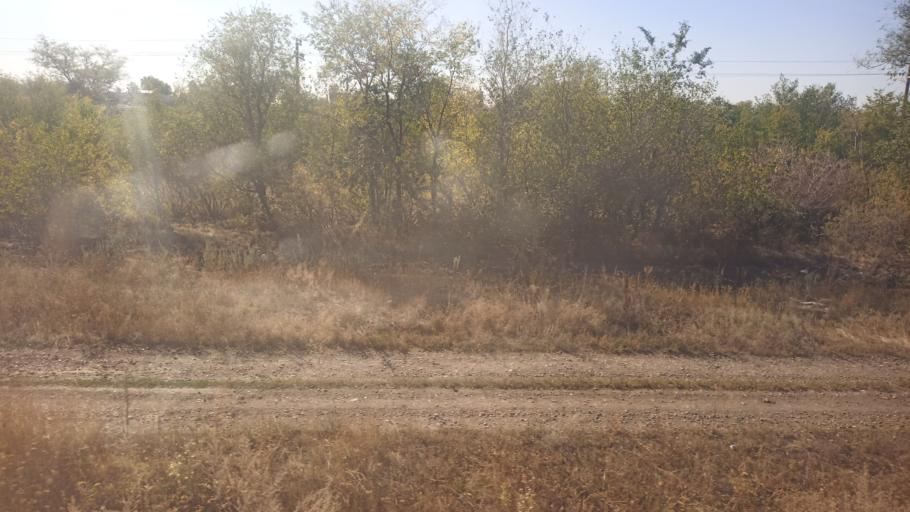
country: RU
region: Saratov
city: Pushkino
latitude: 51.2299
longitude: 46.9854
